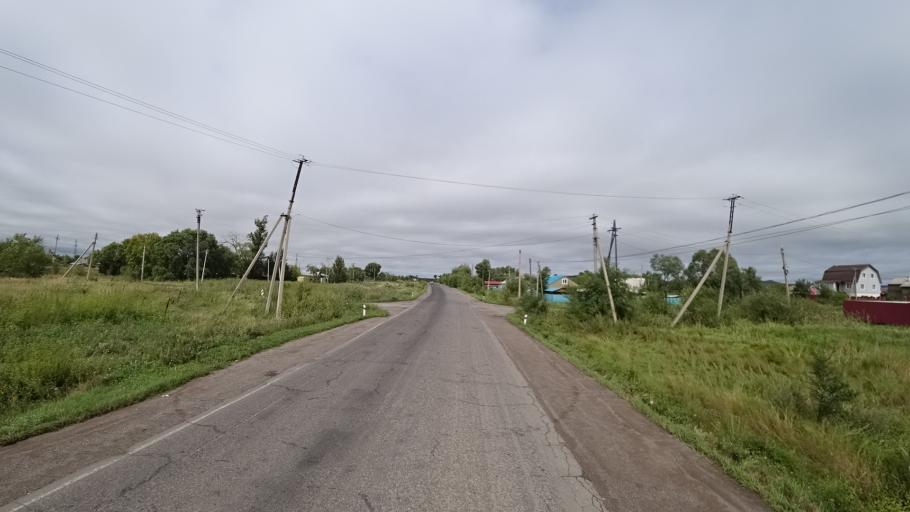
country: RU
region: Primorskiy
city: Monastyrishche
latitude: 44.1958
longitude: 132.4793
